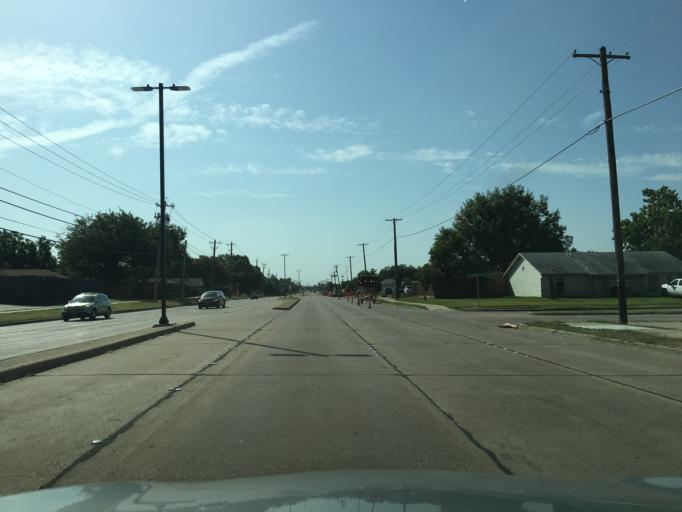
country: US
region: Texas
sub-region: Dallas County
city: Garland
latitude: 32.8718
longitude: -96.6135
